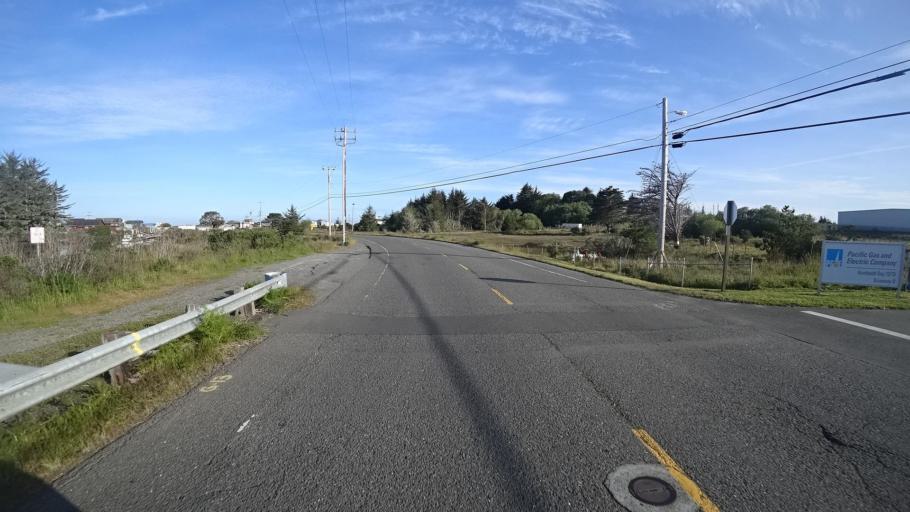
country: US
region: California
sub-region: Humboldt County
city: Humboldt Hill
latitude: 40.7392
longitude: -124.2130
